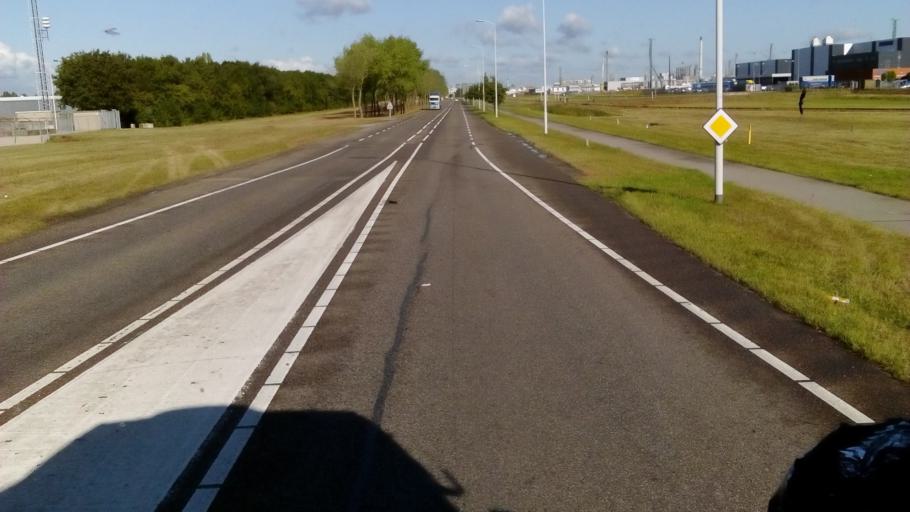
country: NL
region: North Brabant
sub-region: Gemeente Moerdijk
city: Klundert
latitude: 51.6615
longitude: 4.5633
